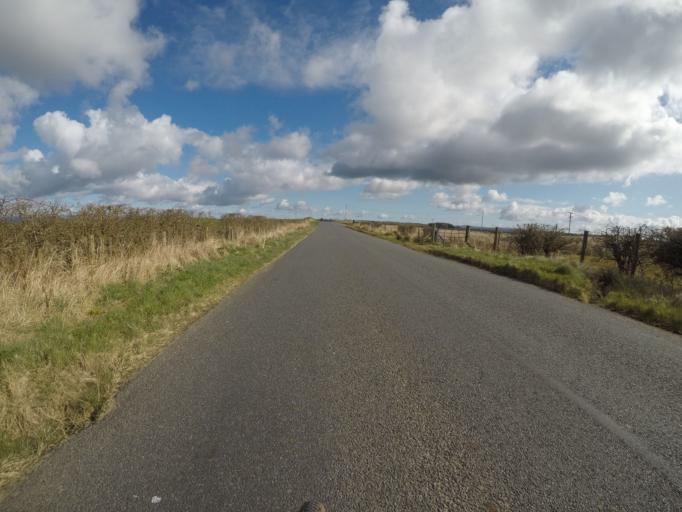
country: GB
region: Scotland
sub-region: North Ayrshire
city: Kilwinning
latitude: 55.6831
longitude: -4.6507
